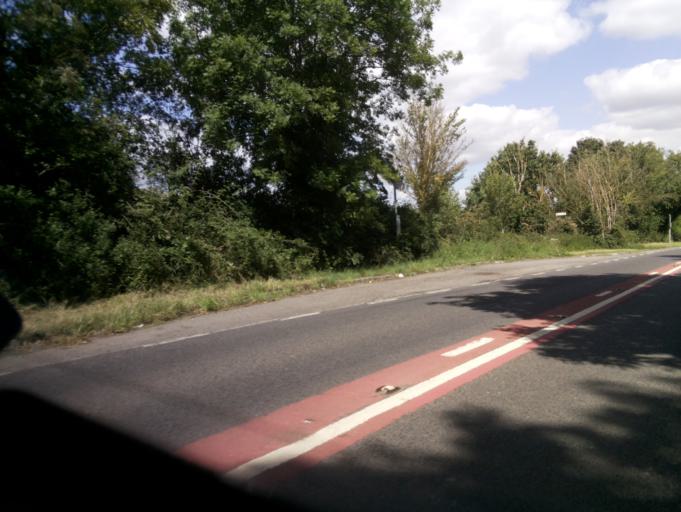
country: GB
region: England
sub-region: Buckinghamshire
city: Aylesbury
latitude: 51.8657
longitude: -0.8335
